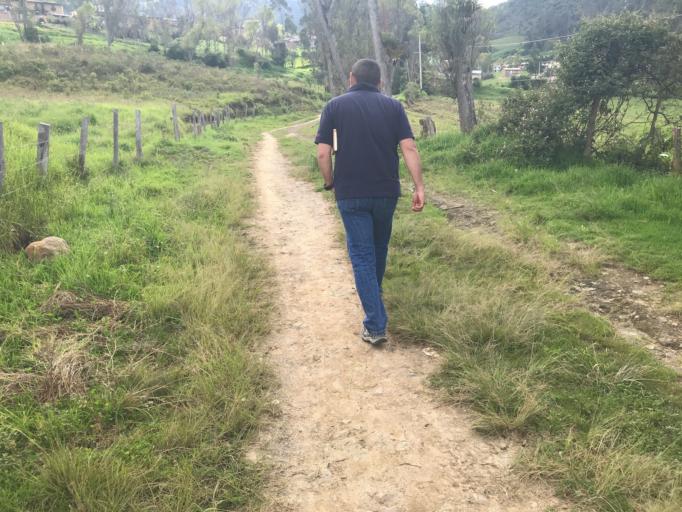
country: PE
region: Cajamarca
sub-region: Provincia de Chota
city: Querocoto
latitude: -6.3589
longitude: -79.0315
